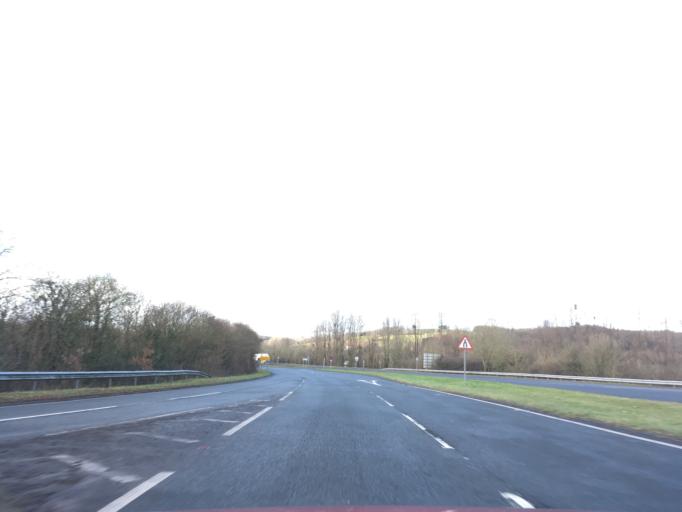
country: GB
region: Wales
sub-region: Monmouthshire
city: Usk
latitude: 51.7046
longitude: -2.8743
